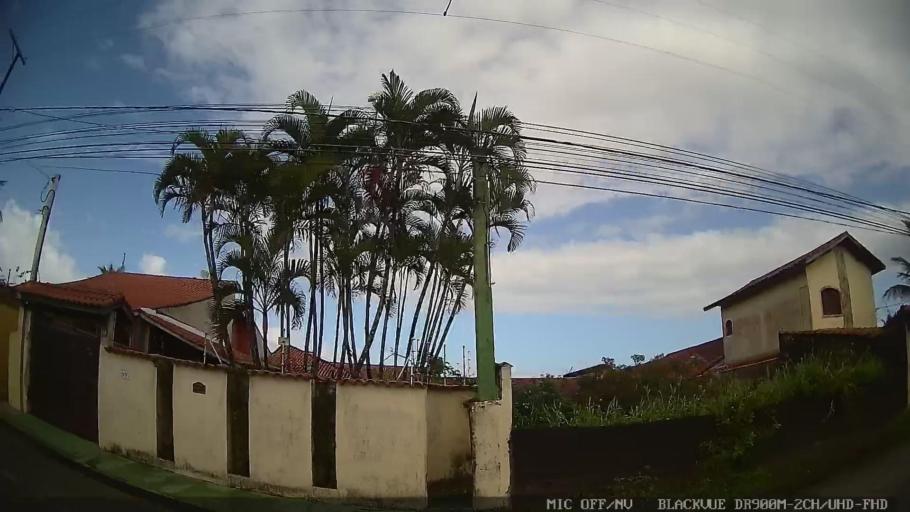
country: BR
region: Sao Paulo
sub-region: Itanhaem
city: Itanhaem
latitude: -24.2071
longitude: -46.8404
